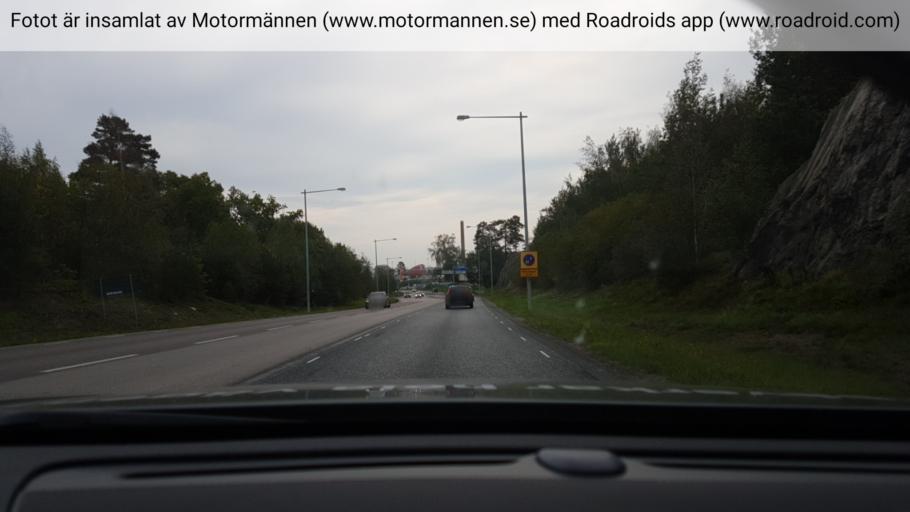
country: SE
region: Stockholm
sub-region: Nynashamns Kommun
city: Nynashamn
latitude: 58.9169
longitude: 17.9564
